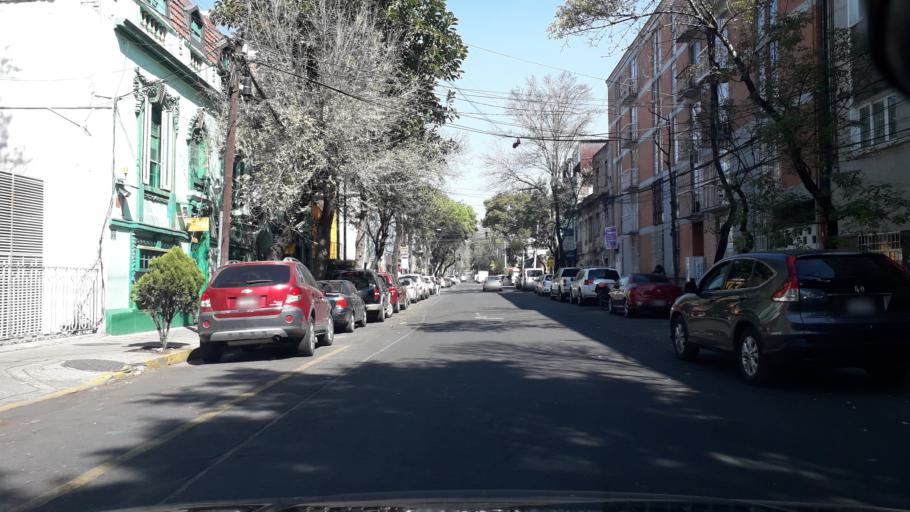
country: MX
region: Mexico City
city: Cuauhtemoc
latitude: 19.4422
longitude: -99.1565
